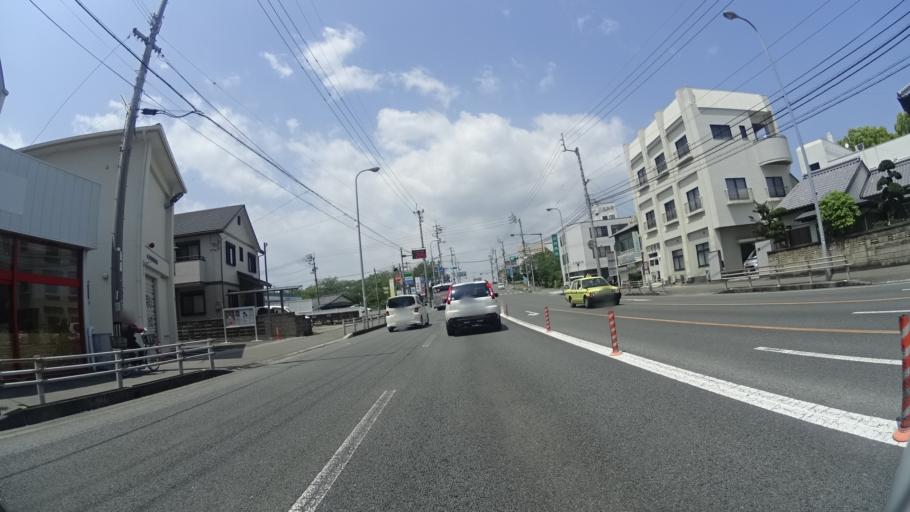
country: JP
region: Tokushima
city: Tokushima-shi
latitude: 34.0719
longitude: 134.5025
